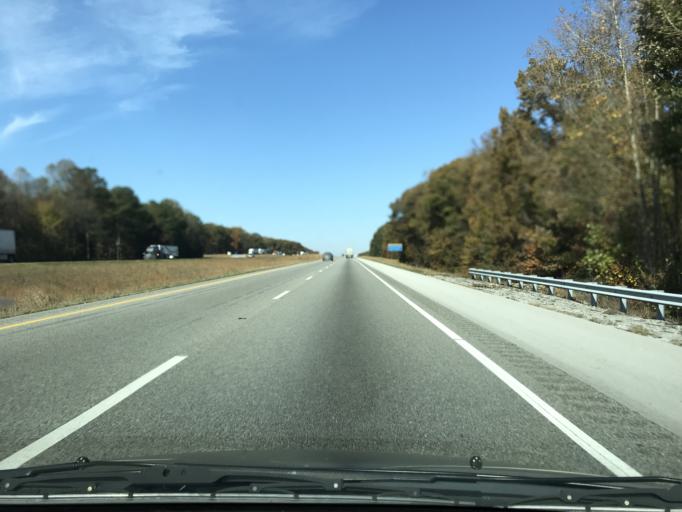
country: US
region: Tennessee
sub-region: Coffee County
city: Manchester
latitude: 35.3862
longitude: -85.9846
